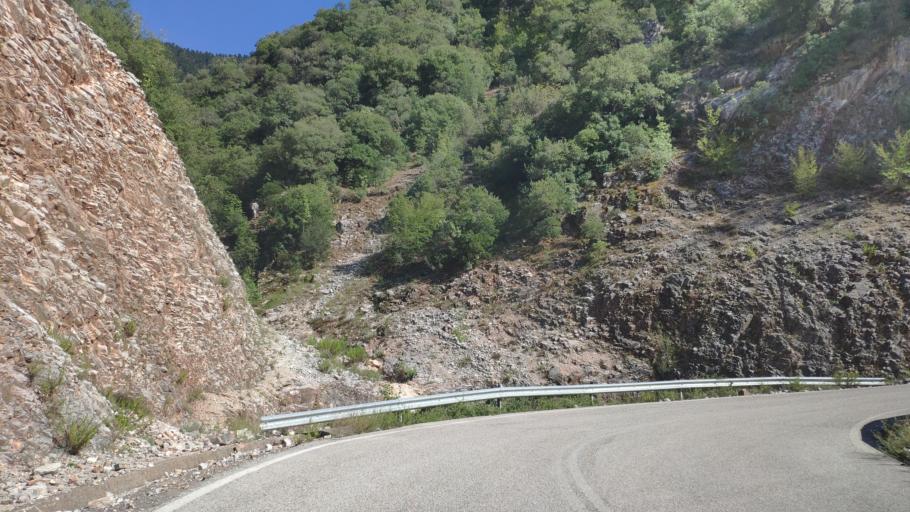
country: GR
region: Central Greece
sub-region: Nomos Evrytanias
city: Kerasochori
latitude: 39.0120
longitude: 21.6008
